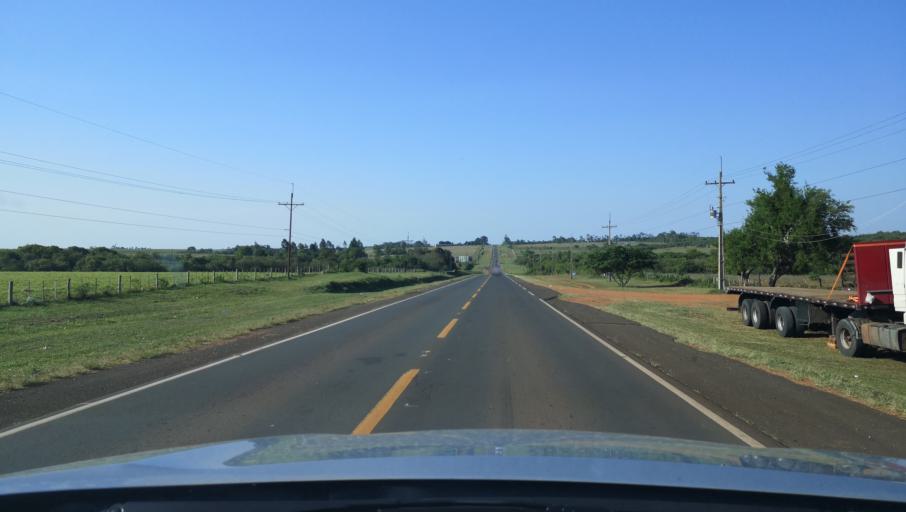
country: PY
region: Misiones
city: Santa Maria
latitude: -26.8369
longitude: -57.0342
